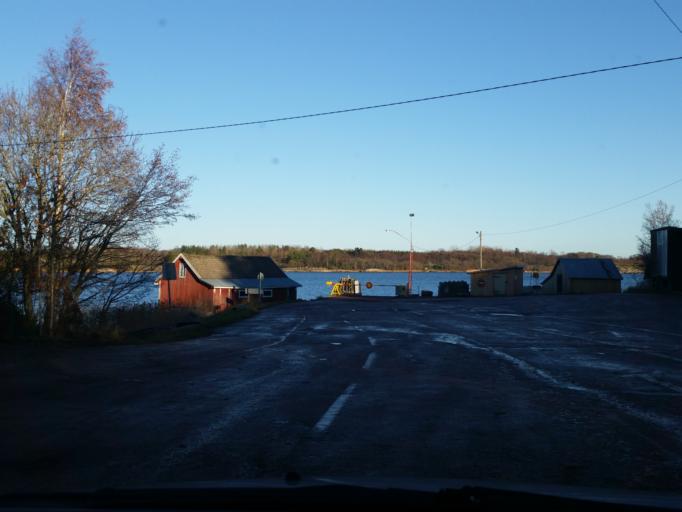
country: AX
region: Alands skaergard
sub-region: Braendoe
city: Braendoe
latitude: 60.3634
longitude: 21.0695
